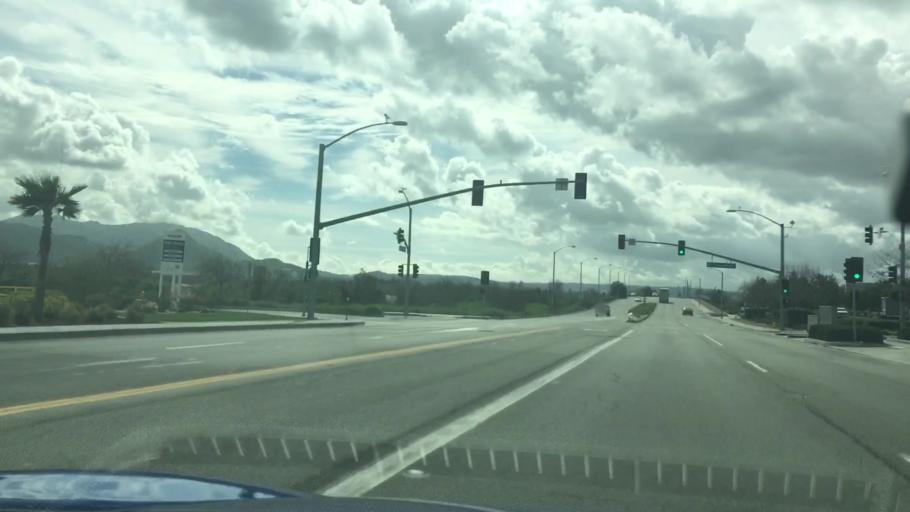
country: US
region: California
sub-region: Riverside County
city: Highgrove
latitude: 34.0312
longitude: -117.3651
